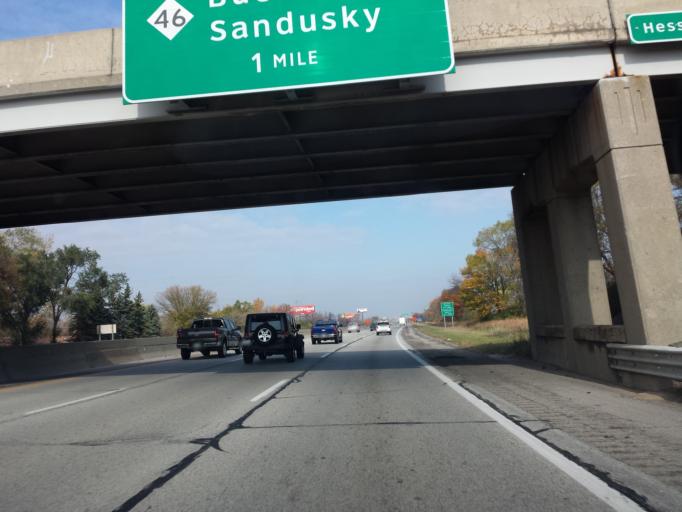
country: US
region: Michigan
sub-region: Saginaw County
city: Buena Vista
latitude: 43.4011
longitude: -83.8910
